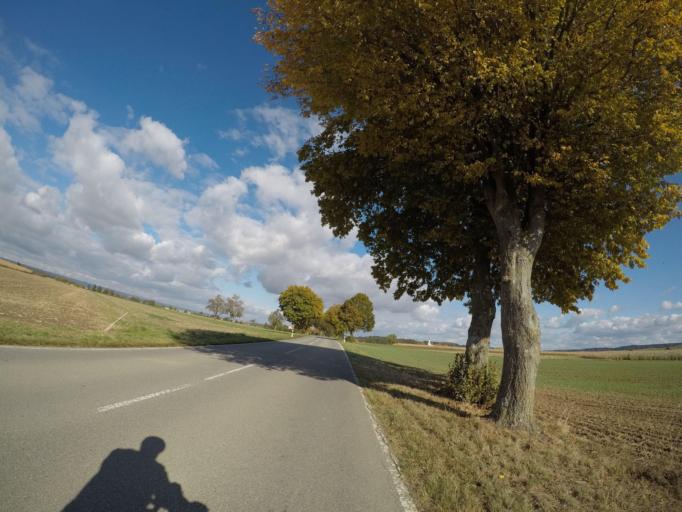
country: DE
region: Baden-Wuerttemberg
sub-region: Tuebingen Region
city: Grundsheim
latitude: 48.1633
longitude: 9.6799
